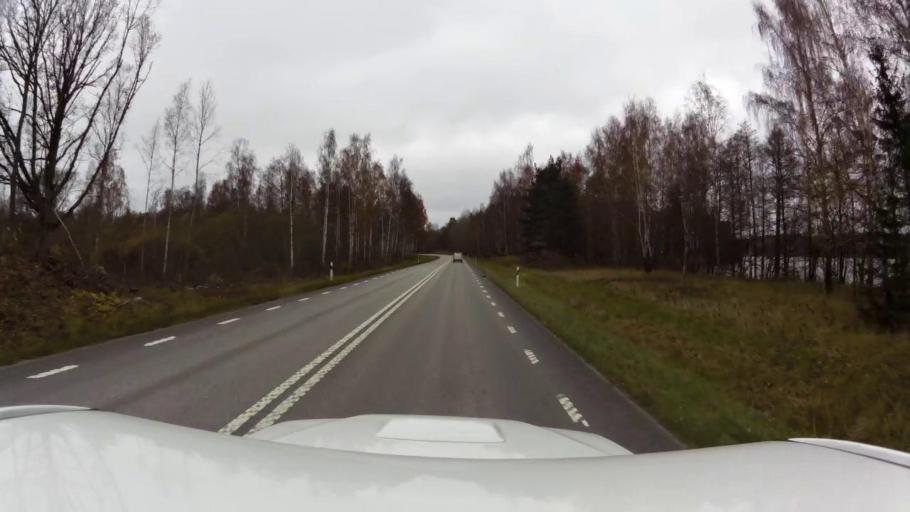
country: SE
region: OEstergoetland
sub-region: Kinda Kommun
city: Rimforsa
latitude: 58.1579
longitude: 15.6805
